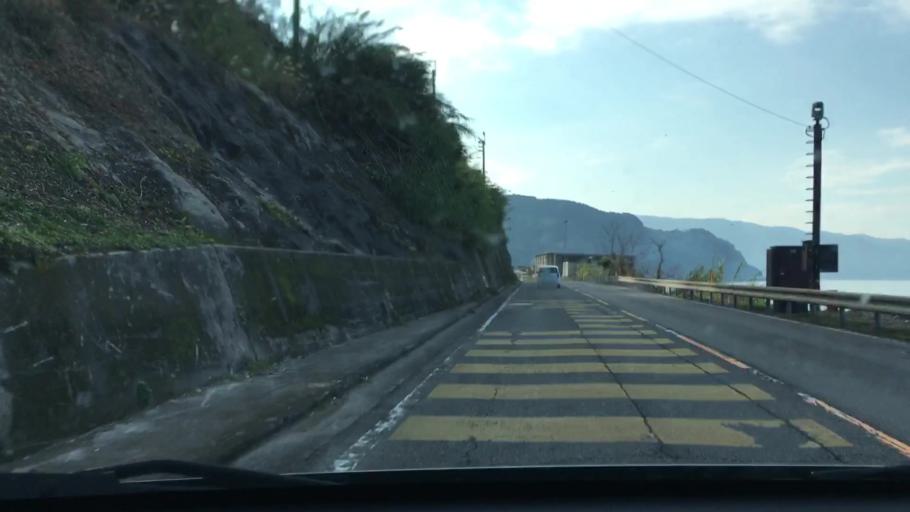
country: JP
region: Kagoshima
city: Hamanoichi
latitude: 31.6207
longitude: 130.7967
